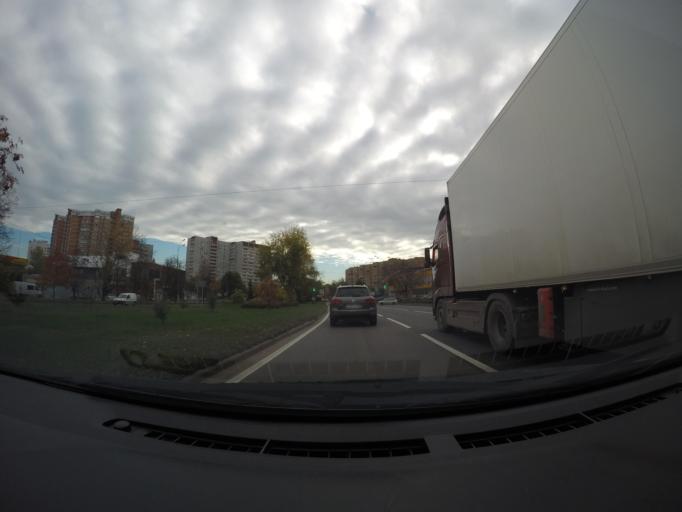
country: RU
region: Moskovskaya
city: Mytishchi
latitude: 55.9262
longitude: 37.7537
